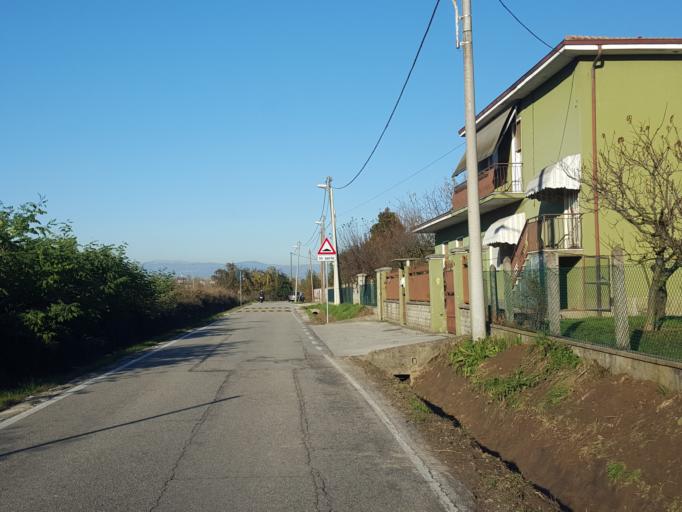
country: IT
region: Veneto
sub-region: Provincia di Vicenza
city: Villaggio Montegrappa
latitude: 45.5297
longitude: 11.6016
